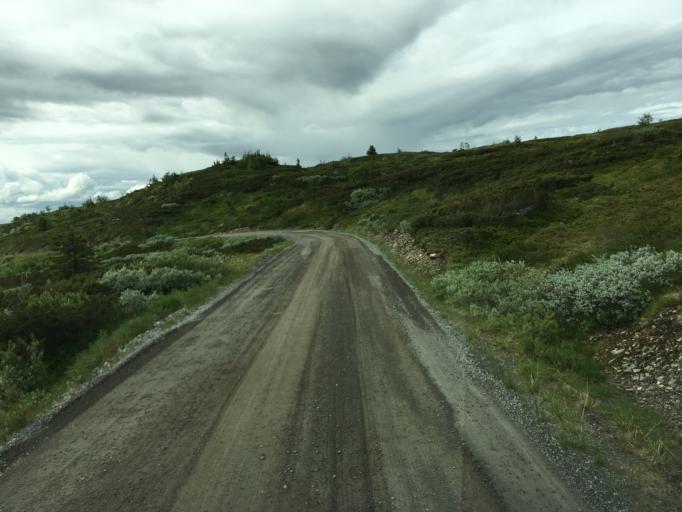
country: NO
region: Oppland
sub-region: Ringebu
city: Ringebu
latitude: 61.3627
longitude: 10.0362
